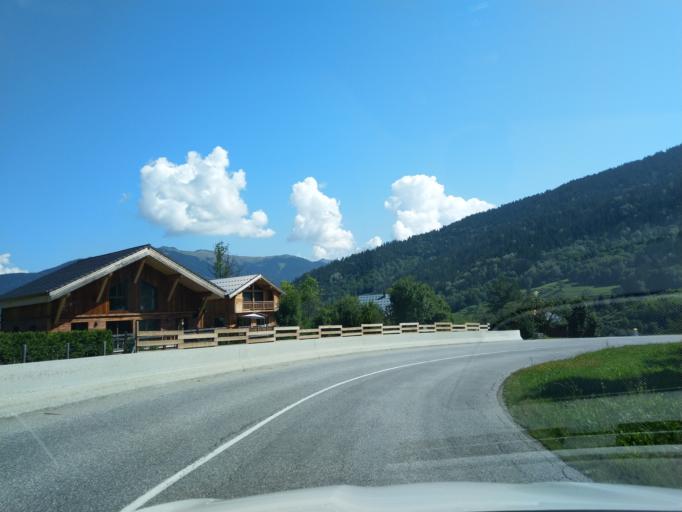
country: FR
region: Rhone-Alpes
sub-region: Departement de la Savoie
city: Les Allues
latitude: 45.4249
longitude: 6.5542
